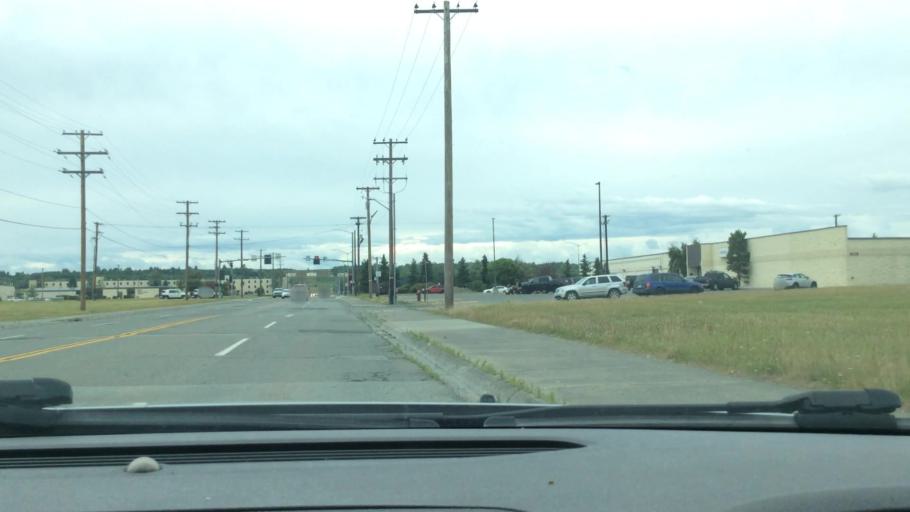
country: US
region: Alaska
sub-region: Anchorage Municipality
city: Anchorage
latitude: 61.2359
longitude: -149.8492
